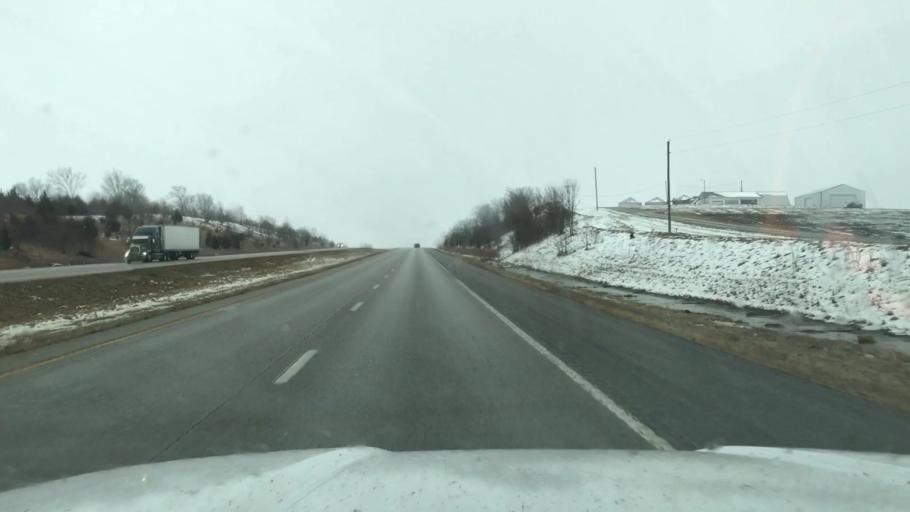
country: US
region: Missouri
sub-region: Buchanan County
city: Saint Joseph
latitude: 39.7477
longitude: -94.7113
